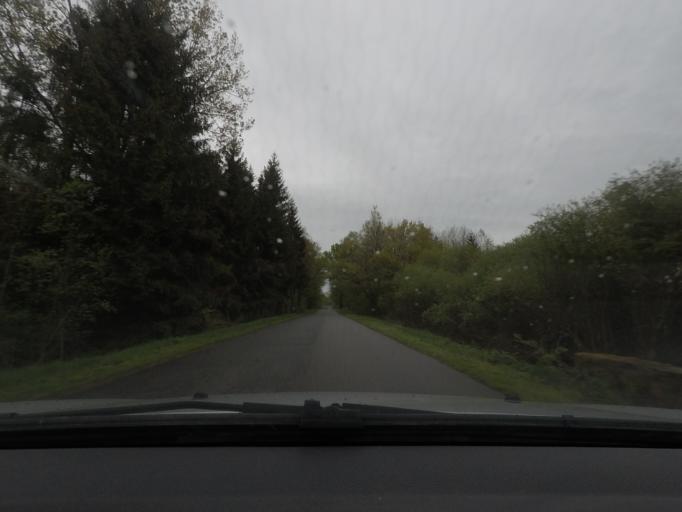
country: BE
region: Wallonia
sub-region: Province du Luxembourg
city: Etalle
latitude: 49.6866
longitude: 5.5632
